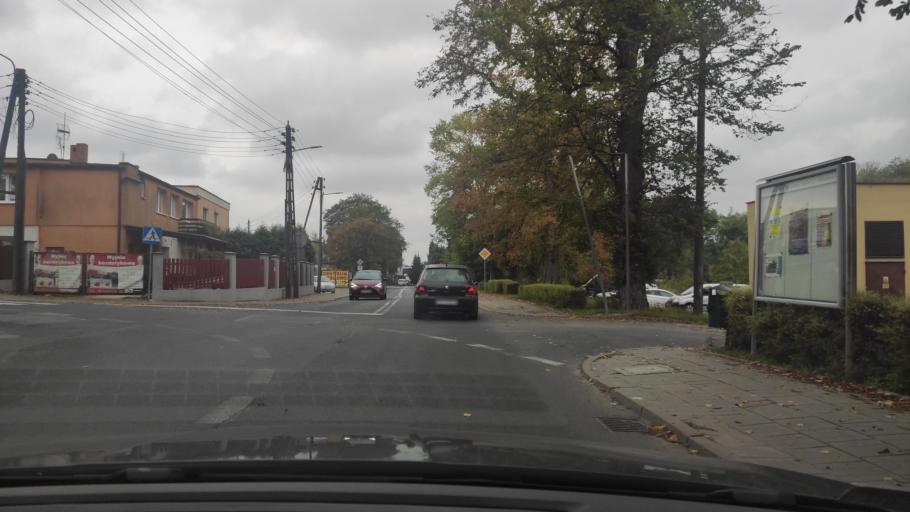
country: PL
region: Greater Poland Voivodeship
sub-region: Powiat poznanski
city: Swarzedz
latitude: 52.4096
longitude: 17.0706
